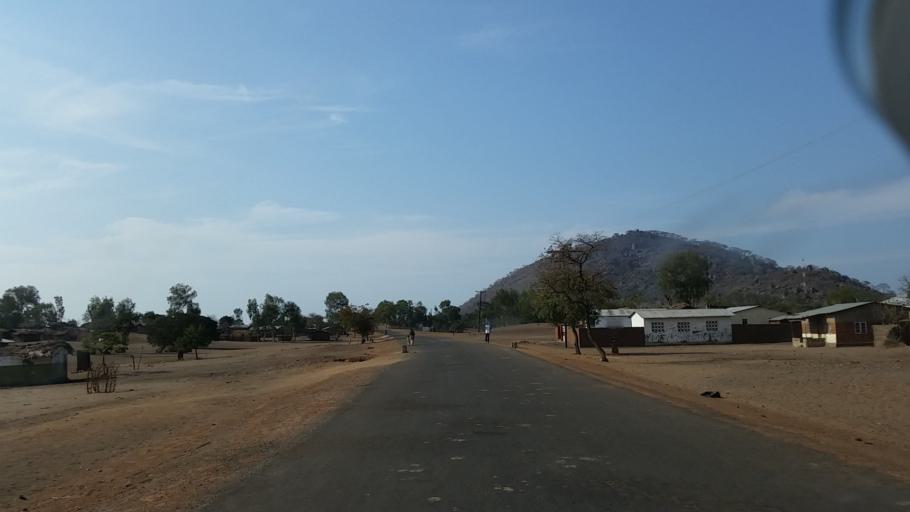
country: MW
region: Central Region
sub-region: Salima District
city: Salima
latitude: -13.6922
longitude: 34.5886
